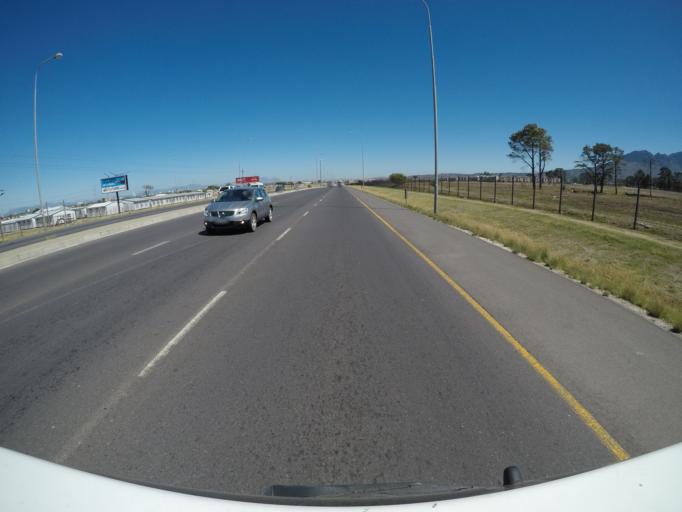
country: ZA
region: Western Cape
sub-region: Overberg District Municipality
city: Grabouw
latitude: -34.1127
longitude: 18.8686
